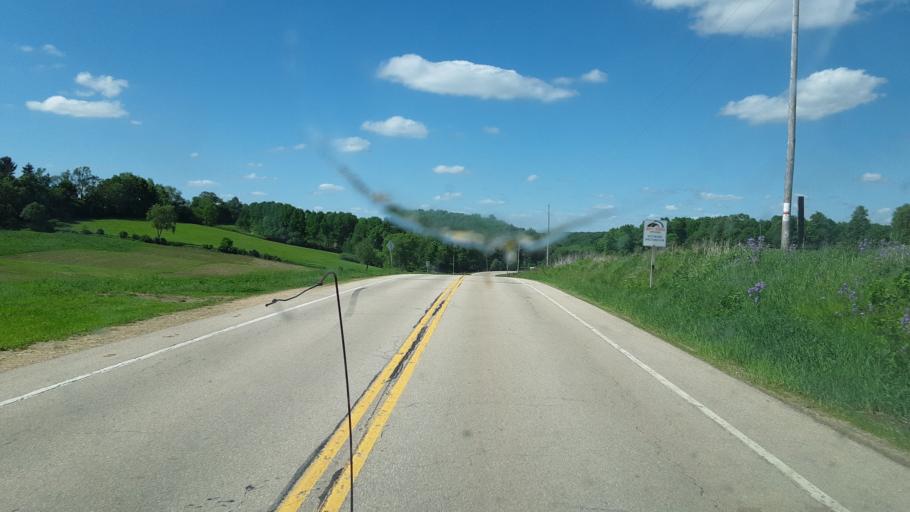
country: US
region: Wisconsin
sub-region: Sauk County
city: Reedsburg
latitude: 43.4795
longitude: -90.2046
